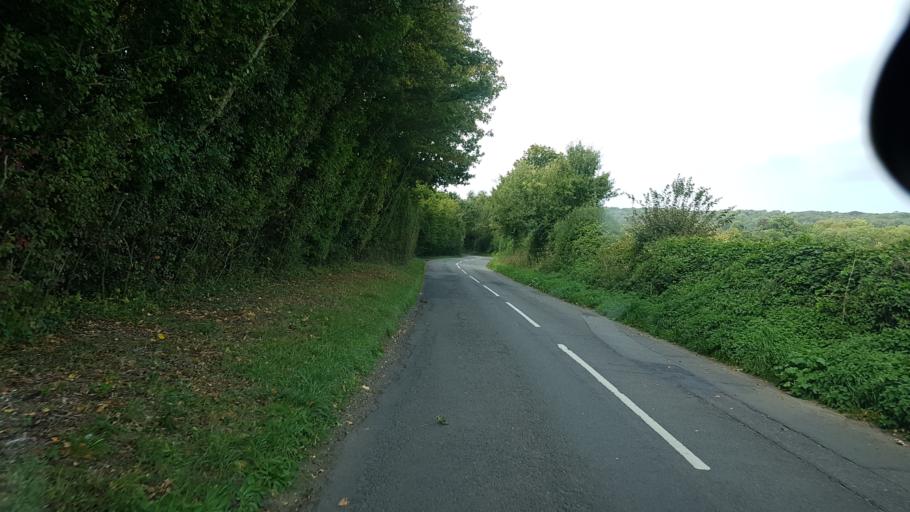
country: GB
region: England
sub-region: Kent
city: West Malling
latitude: 51.3132
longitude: 0.3599
